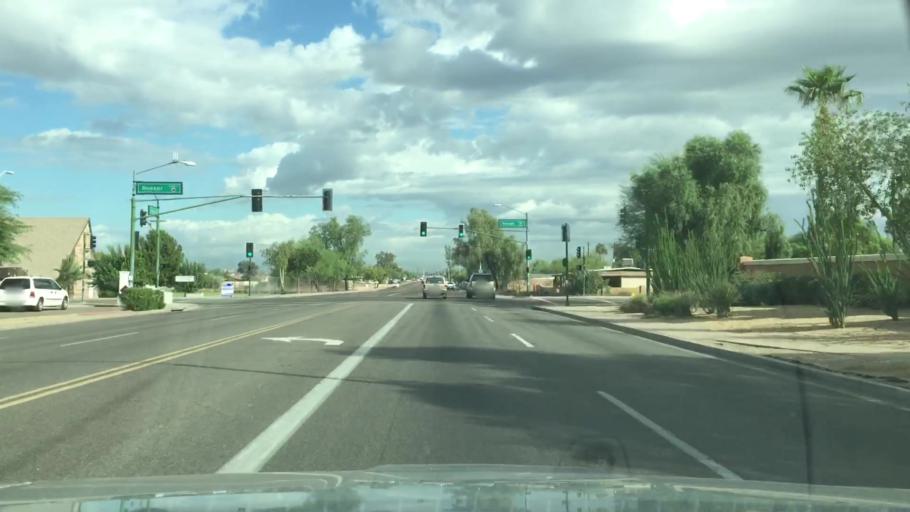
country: US
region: Arizona
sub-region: Maricopa County
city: Phoenix
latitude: 33.3990
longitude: -112.0992
